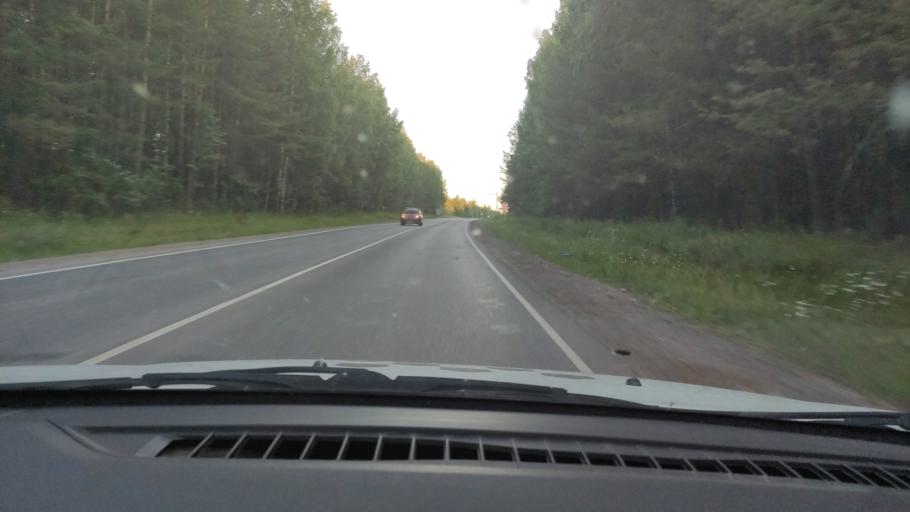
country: RU
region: Perm
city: Kungur
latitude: 57.4128
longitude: 56.9116
